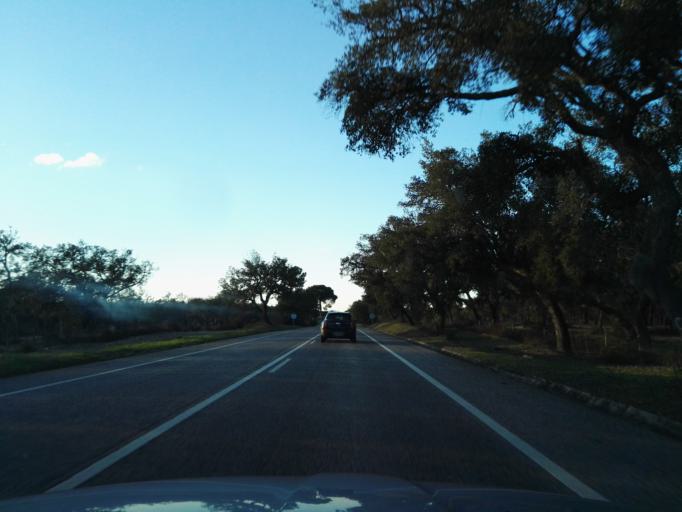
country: PT
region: Santarem
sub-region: Benavente
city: Poceirao
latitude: 38.8780
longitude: -8.8108
